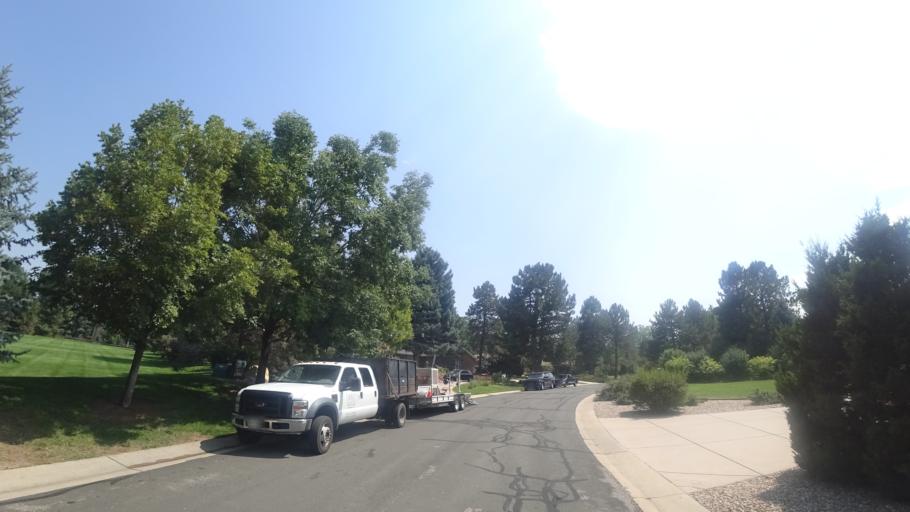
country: US
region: Colorado
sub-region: Arapahoe County
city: Greenwood Village
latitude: 39.6212
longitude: -104.9669
